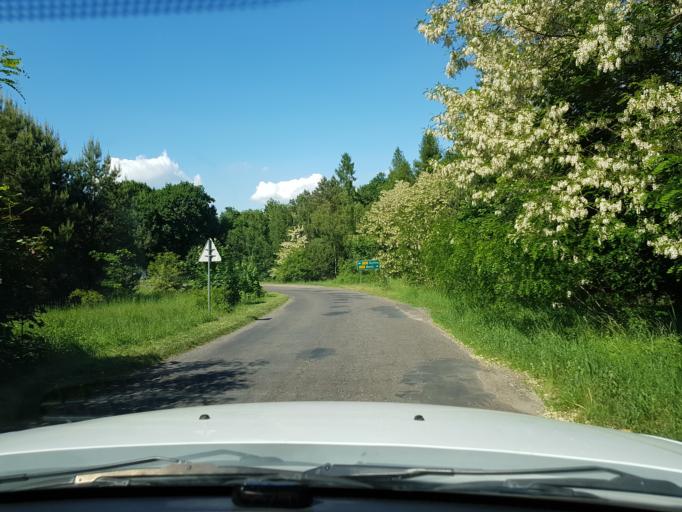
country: PL
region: West Pomeranian Voivodeship
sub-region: Powiat gryfinski
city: Gryfino
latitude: 53.1803
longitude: 14.5493
